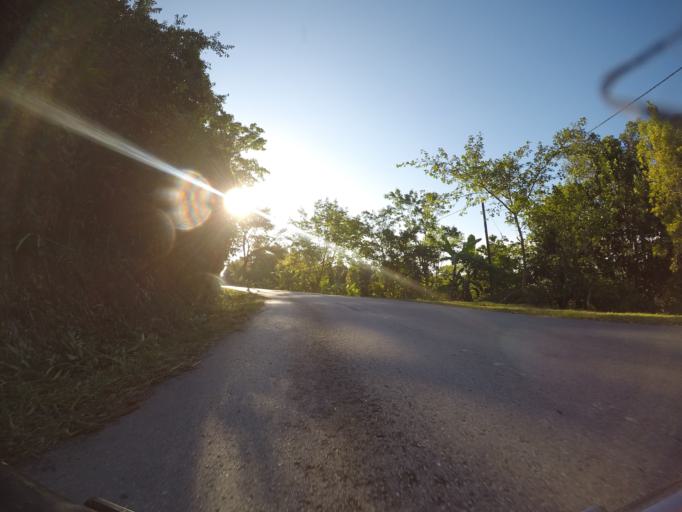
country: TZ
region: Pemba South
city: Mtambile
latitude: -5.3776
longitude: 39.6893
